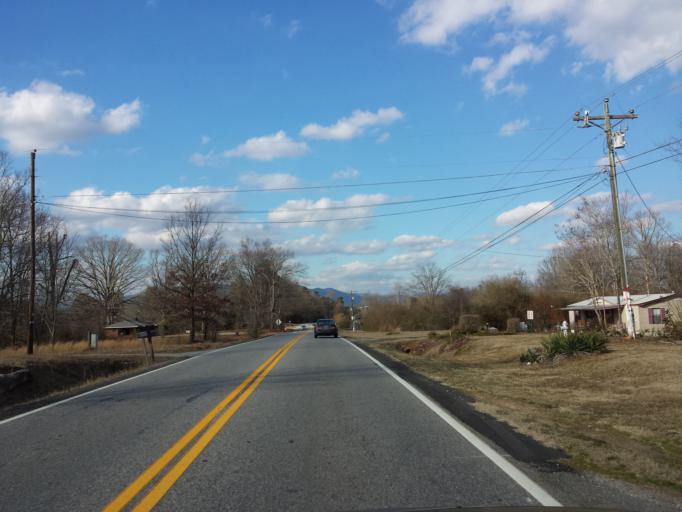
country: US
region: Georgia
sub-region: White County
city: Cleveland
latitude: 34.5813
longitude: -83.7911
